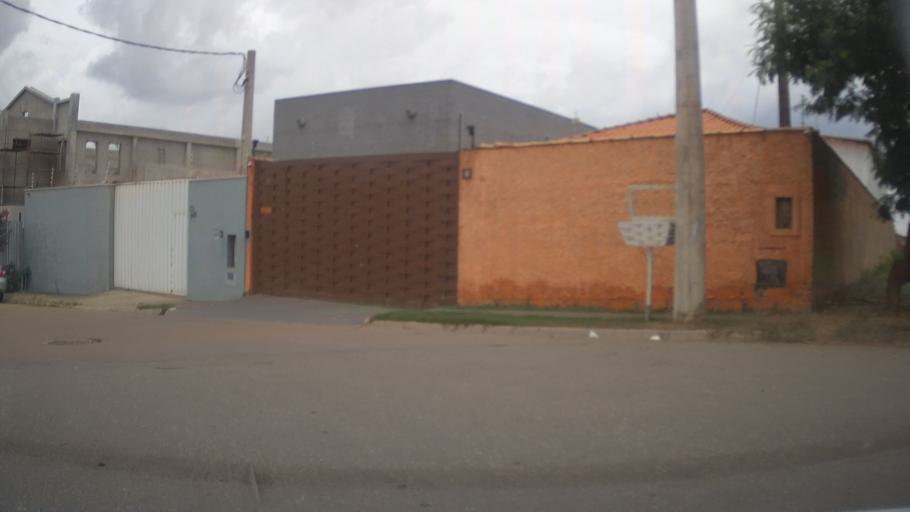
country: BR
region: Sao Paulo
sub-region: Itupeva
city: Itupeva
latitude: -23.1506
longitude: -47.0029
